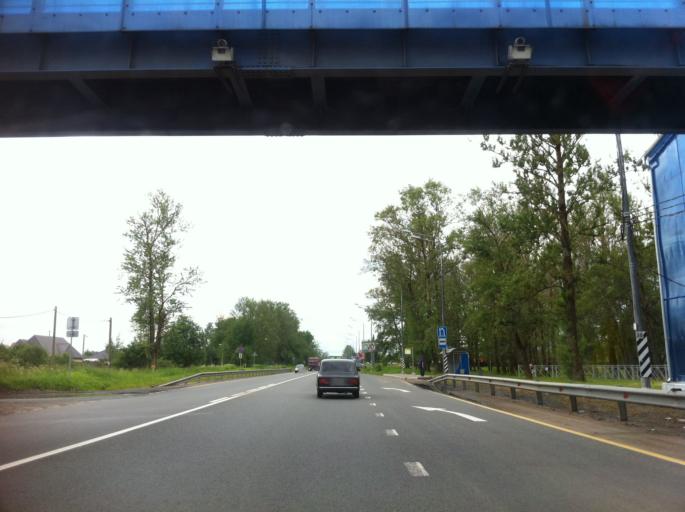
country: RU
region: Leningrad
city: Maloye Verevo
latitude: 59.6137
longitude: 30.1733
